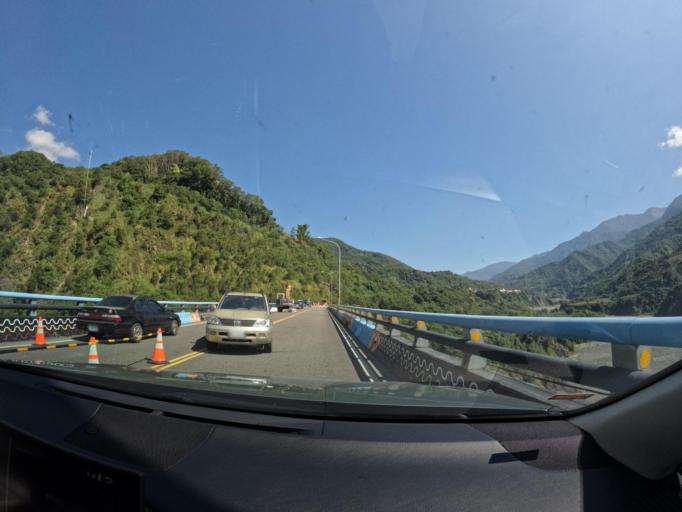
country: TW
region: Taiwan
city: Yujing
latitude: 23.1496
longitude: 120.7566
